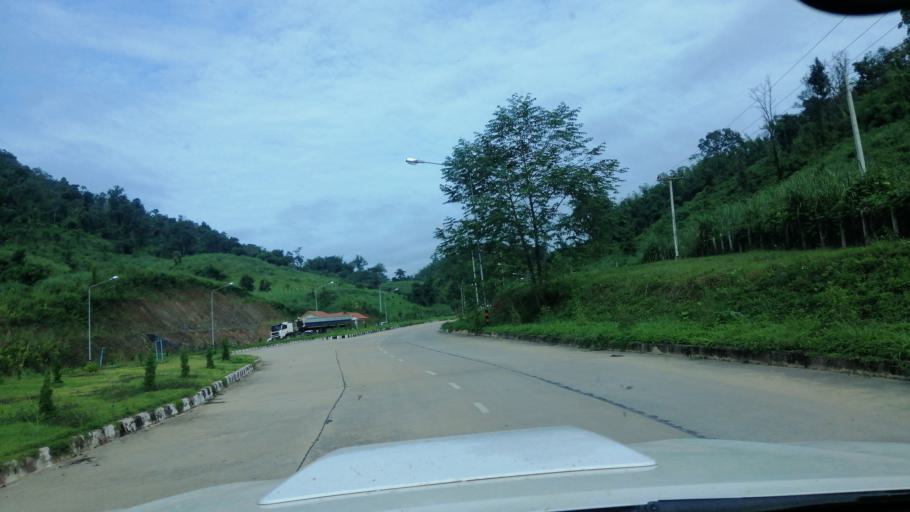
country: TH
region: Phayao
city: Phu Sang
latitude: 19.6760
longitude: 100.4372
